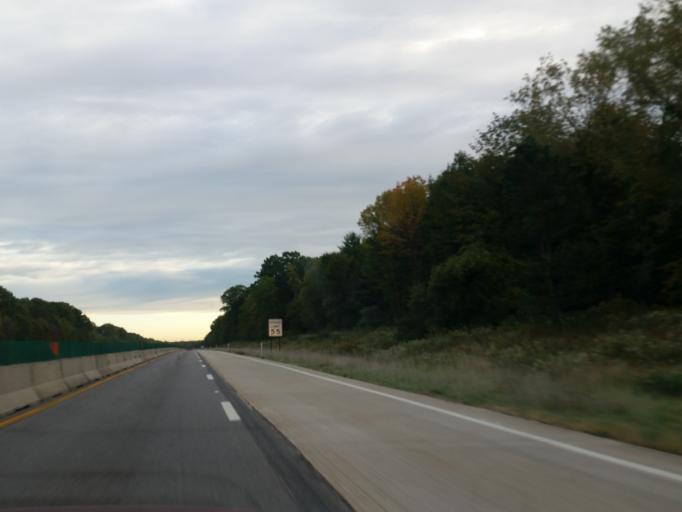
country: US
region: Ohio
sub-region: Ashtabula County
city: Ashtabula
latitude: 41.8173
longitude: -80.8044
